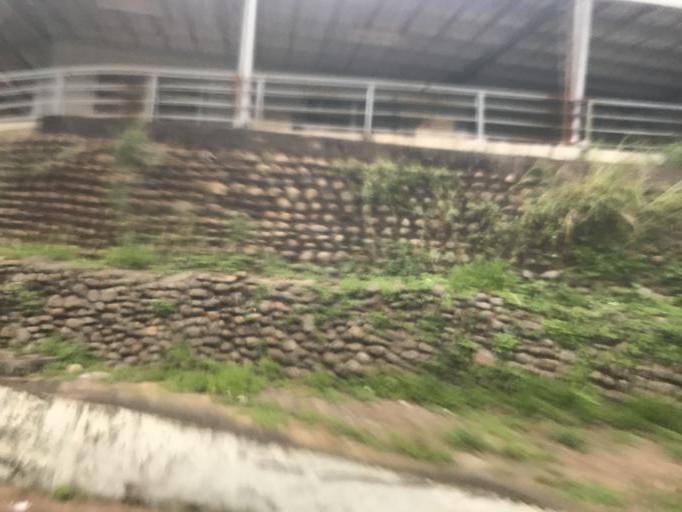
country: TW
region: Taiwan
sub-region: Hsinchu
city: Hsinchu
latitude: 24.7798
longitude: 120.9352
